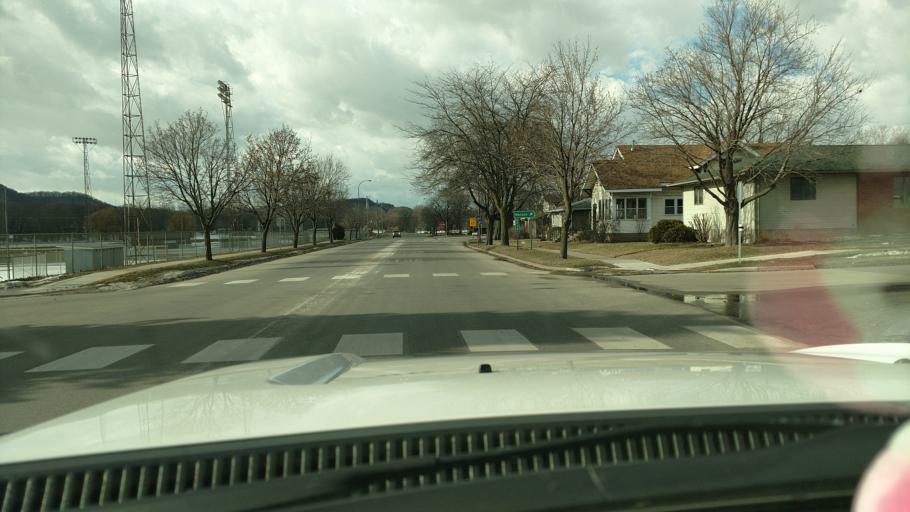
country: US
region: Minnesota
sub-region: Wabasha County
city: Wabasha
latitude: 44.3812
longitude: -92.0351
